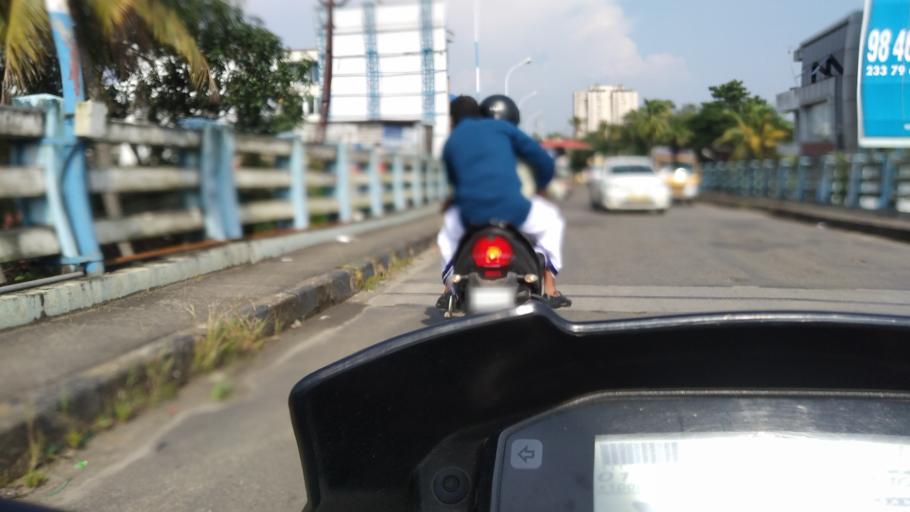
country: IN
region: Kerala
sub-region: Ernakulam
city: Cochin
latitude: 9.9828
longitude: 76.2895
